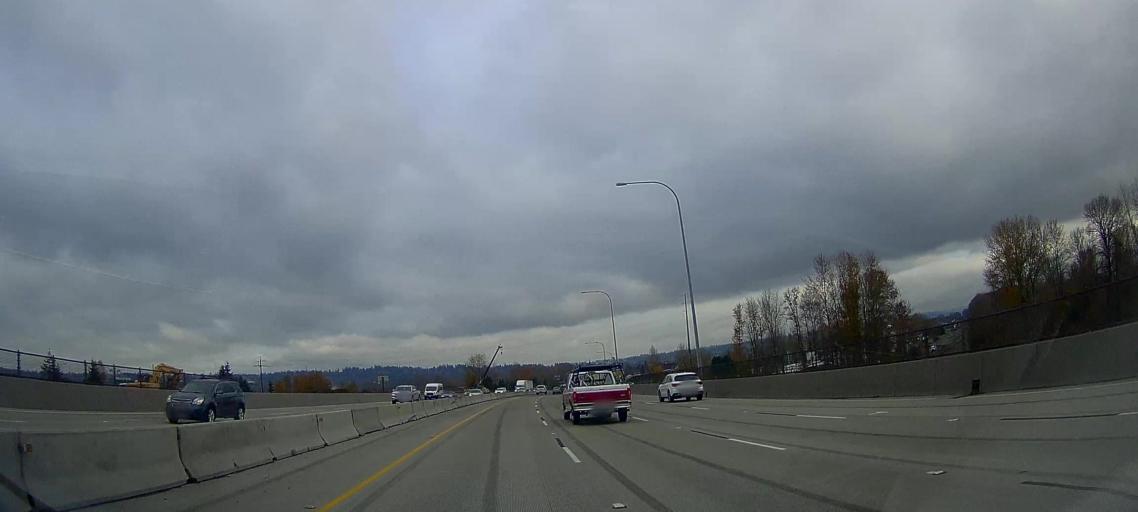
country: US
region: Washington
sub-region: Pierce County
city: Fife
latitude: 47.2409
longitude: -122.3966
